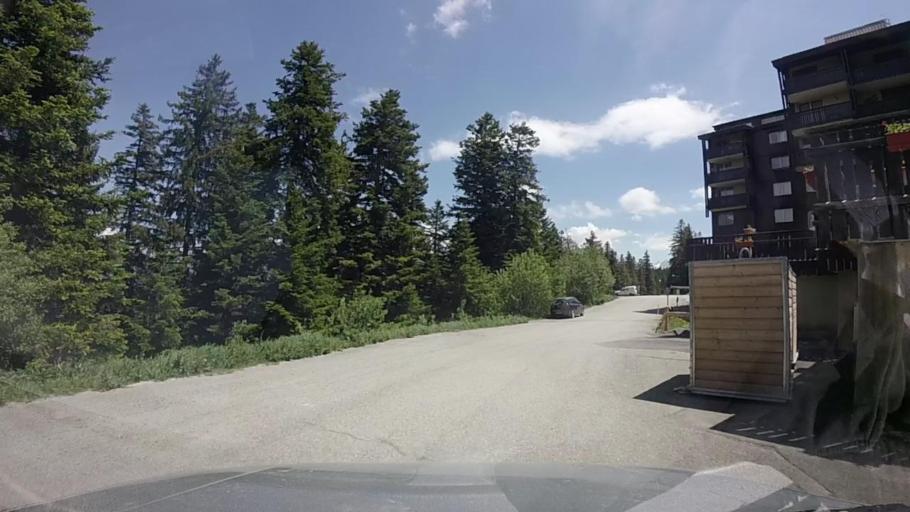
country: FR
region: Provence-Alpes-Cote d'Azur
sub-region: Departement des Alpes-de-Haute-Provence
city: Seyne-les-Alpes
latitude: 44.3477
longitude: 6.2929
